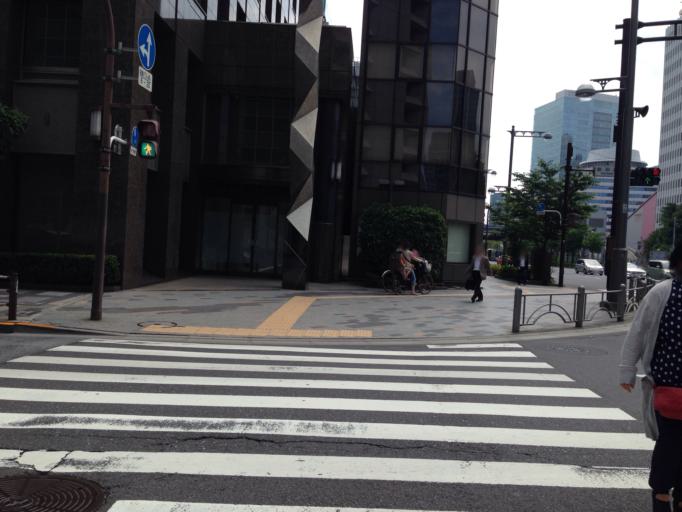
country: JP
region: Tokyo
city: Tokyo
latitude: 35.6771
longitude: 139.7672
